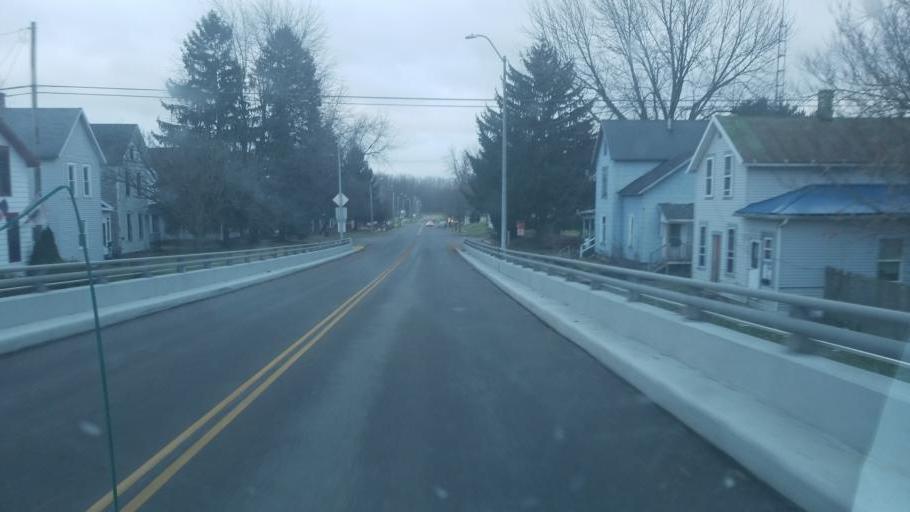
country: US
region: Ohio
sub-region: Crawford County
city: Galion
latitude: 40.7351
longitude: -82.7812
